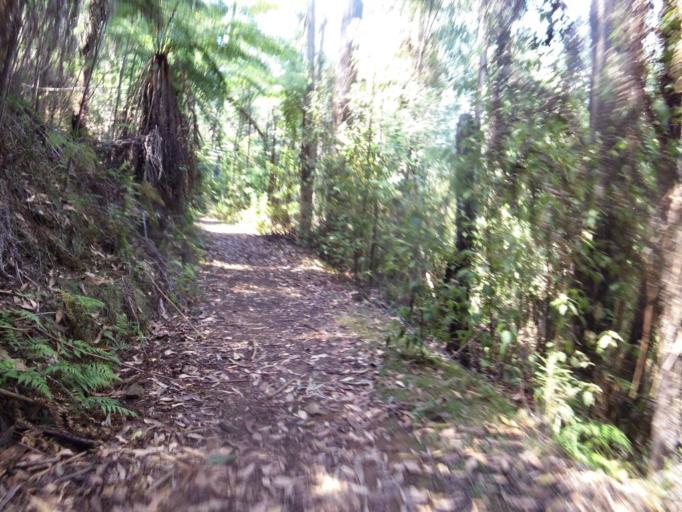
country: AU
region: Victoria
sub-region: Murrindindi
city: Alexandra
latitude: -37.3988
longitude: 145.5602
